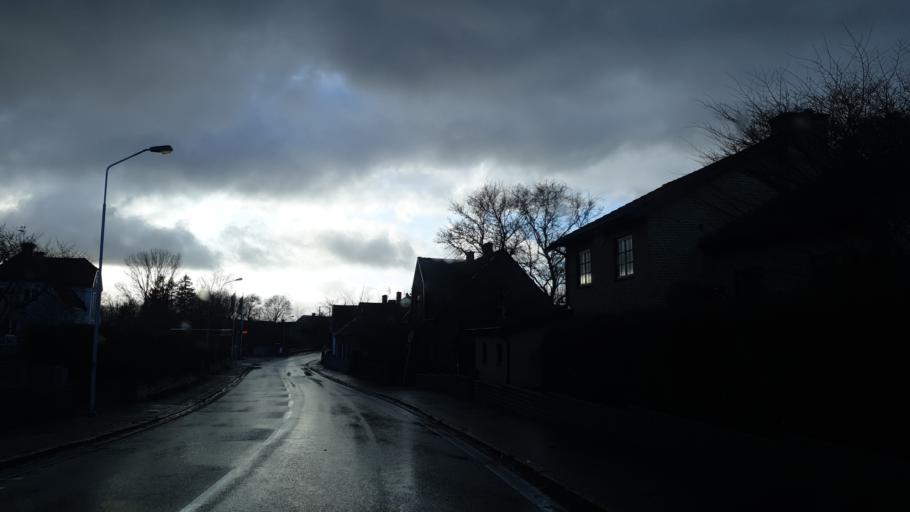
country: SE
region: Skane
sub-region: Skurups Kommun
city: Rydsgard
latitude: 55.4754
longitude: 13.5924
